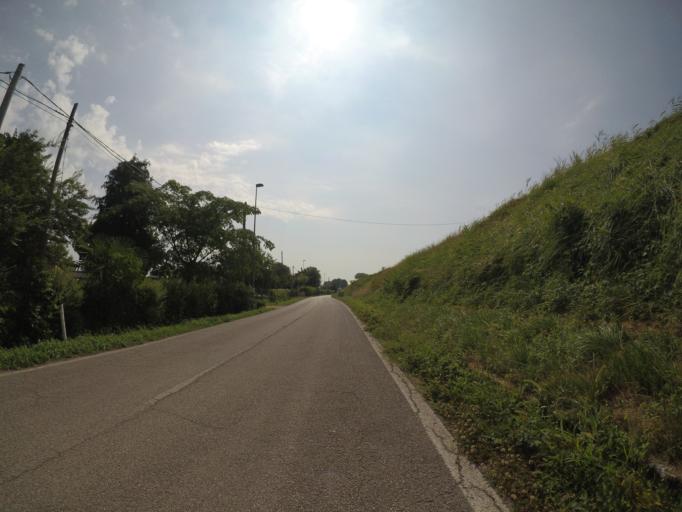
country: IT
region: Friuli Venezia Giulia
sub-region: Provincia di Udine
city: Pertegada
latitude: 45.7061
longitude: 13.0441
